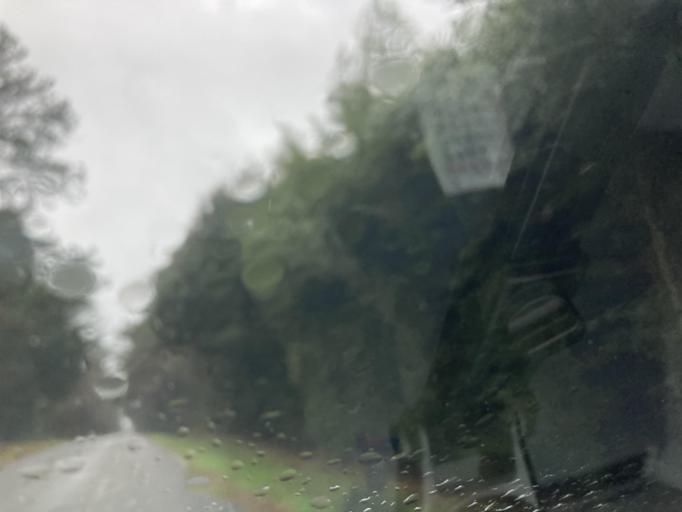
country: US
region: Mississippi
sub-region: Forrest County
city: Rawls Springs
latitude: 31.4816
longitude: -89.3952
